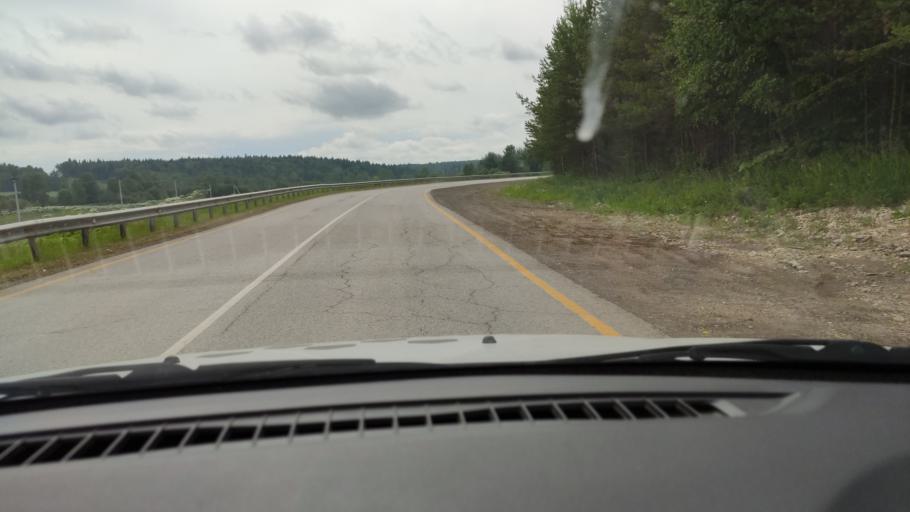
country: RU
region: Perm
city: Kukushtan
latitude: 57.4891
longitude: 56.6295
